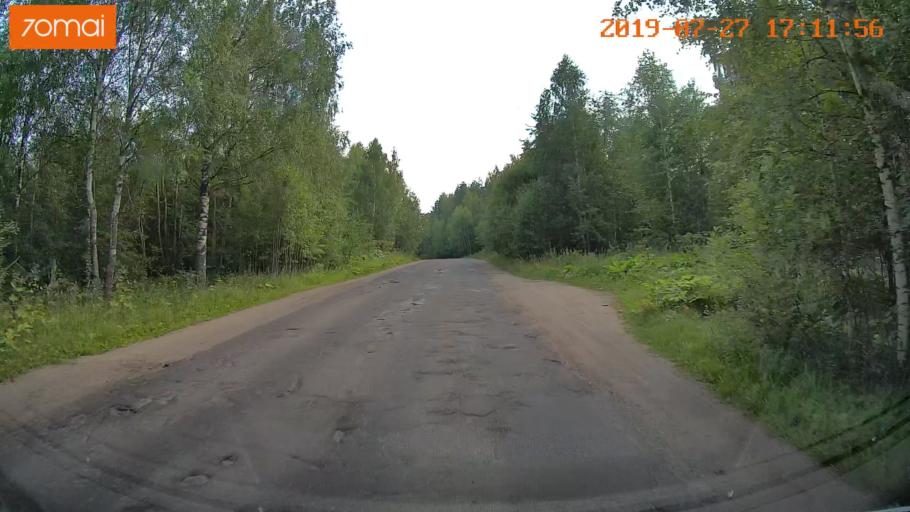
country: RU
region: Ivanovo
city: Novo-Talitsy
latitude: 57.0617
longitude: 40.8637
